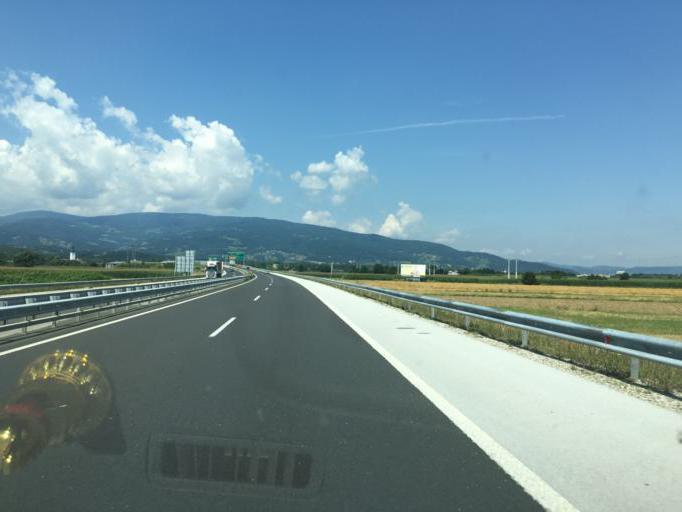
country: SI
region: Hoce-Slivnica
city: Hotinja Vas
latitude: 46.4763
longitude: 15.6719
